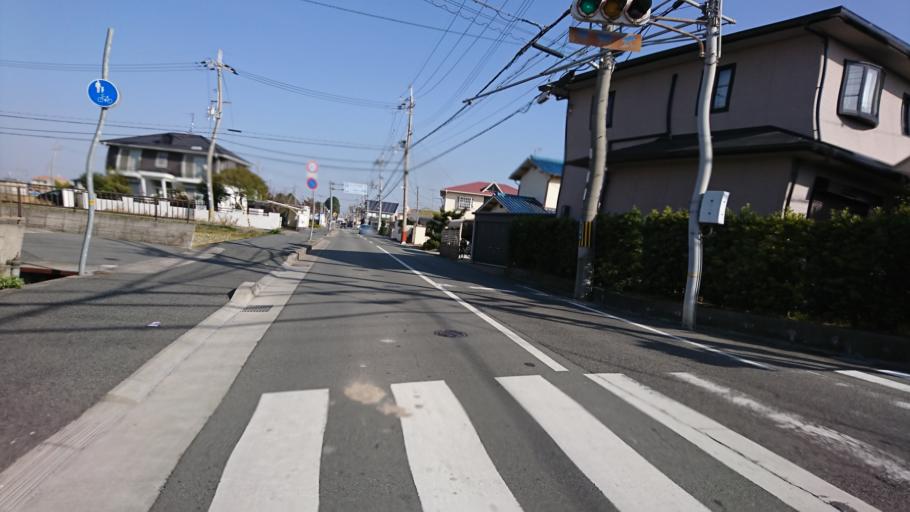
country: JP
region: Hyogo
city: Kakogawacho-honmachi
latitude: 34.7243
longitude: 134.8733
